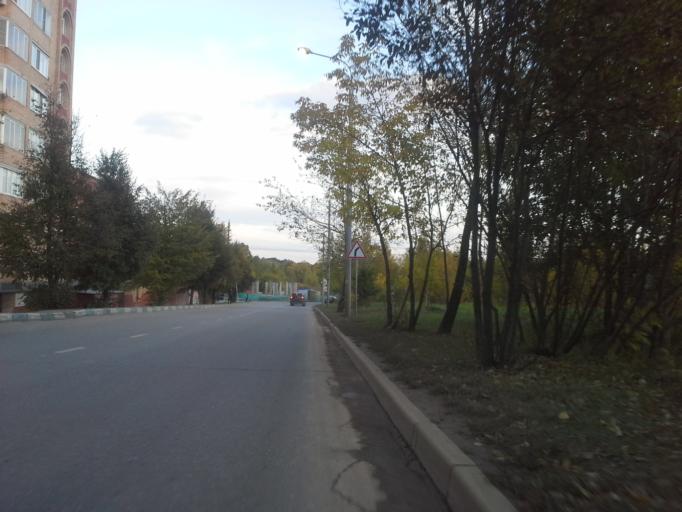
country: RU
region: Moskovskaya
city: Kommunarka
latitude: 55.5795
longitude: 37.4817
